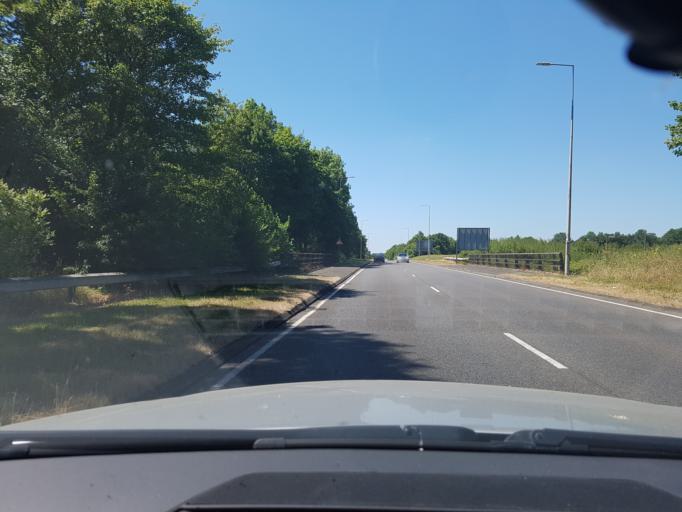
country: GB
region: England
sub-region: Milton Keynes
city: Milton Keynes
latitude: 52.0497
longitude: -0.7677
